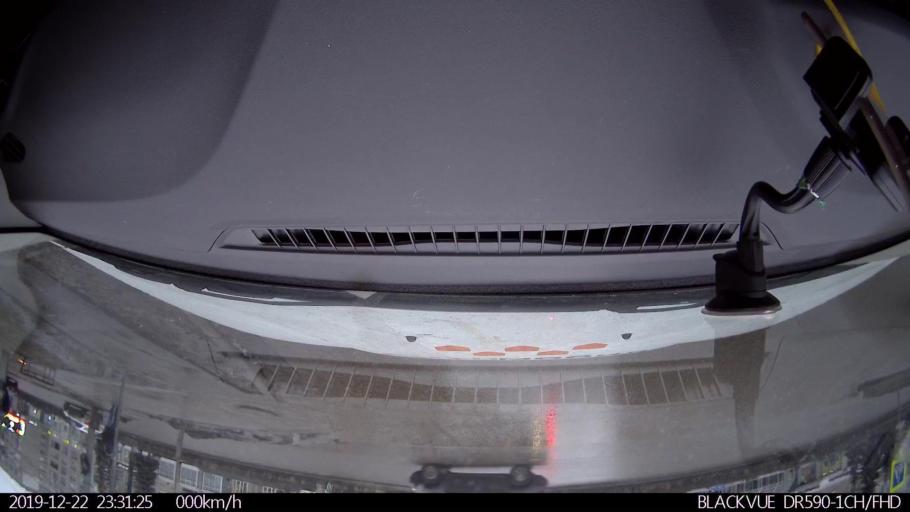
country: RU
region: Nizjnij Novgorod
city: Gorbatovka
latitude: 56.2398
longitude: 43.8650
